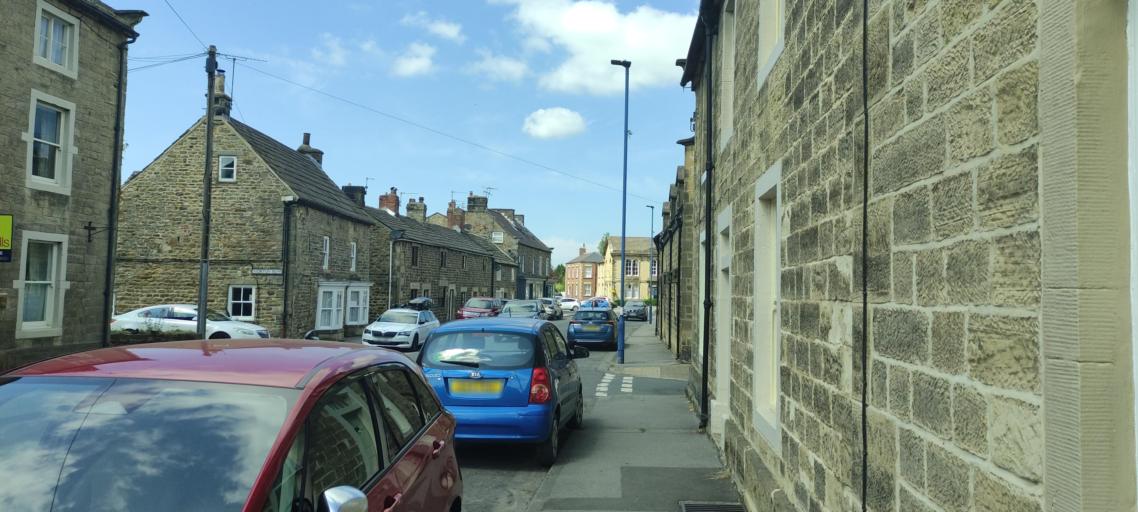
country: GB
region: England
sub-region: North Yorkshire
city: Bedale
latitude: 54.2208
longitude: -1.6580
